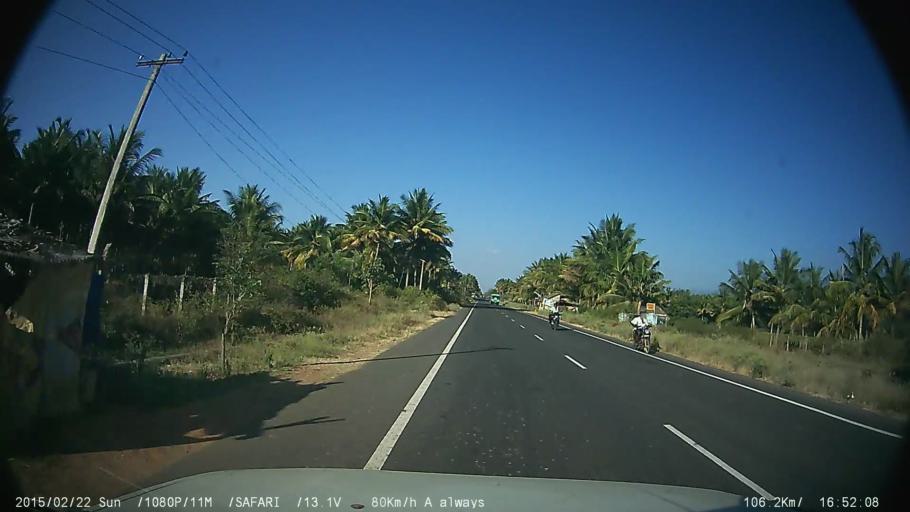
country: IN
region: Tamil Nadu
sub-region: Theni
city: Gudalur
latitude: 9.6554
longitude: 77.2225
